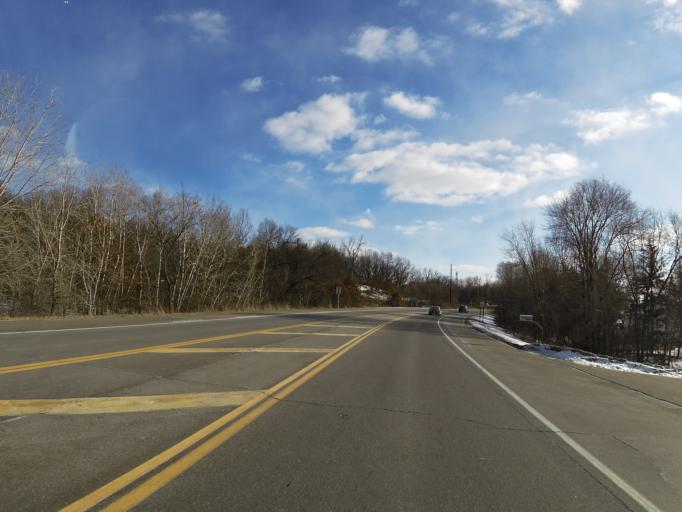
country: US
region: Minnesota
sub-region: Dakota County
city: Eagan
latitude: 44.8034
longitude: -93.1059
